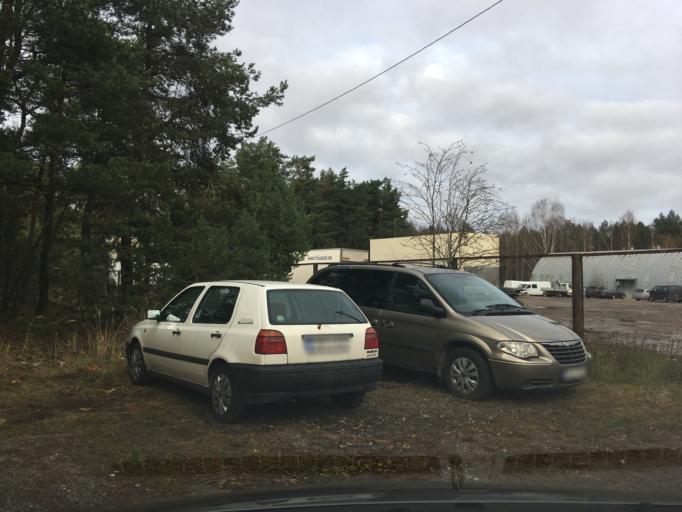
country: EE
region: Harju
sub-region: Saue vald
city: Laagri
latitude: 59.3586
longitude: 24.6329
